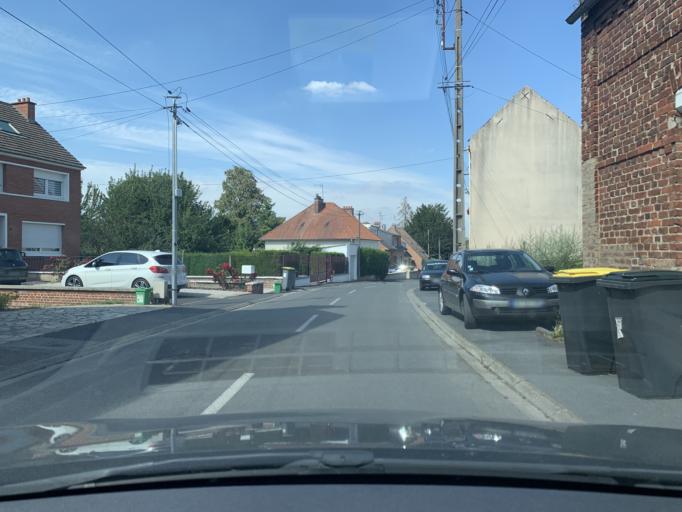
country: FR
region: Nord-Pas-de-Calais
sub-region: Departement du Nord
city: Cambrai
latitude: 50.1640
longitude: 3.2316
